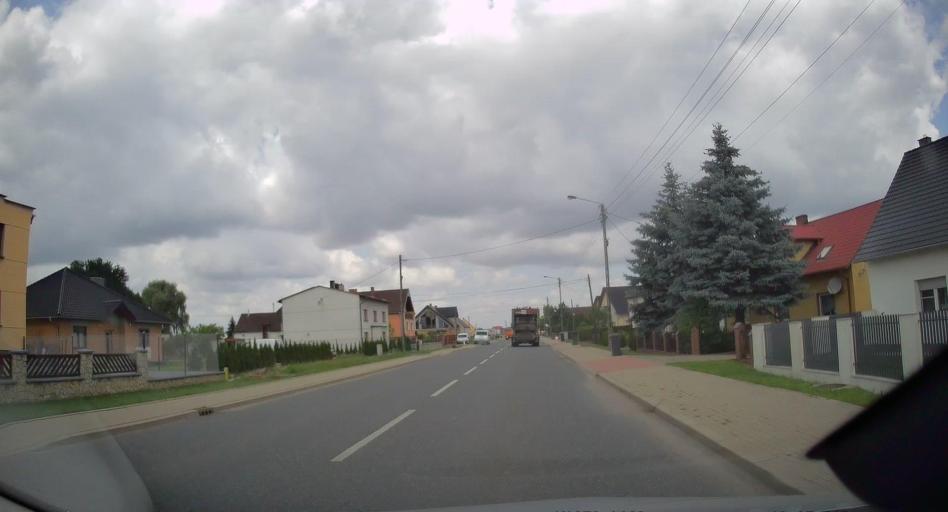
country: PL
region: Opole Voivodeship
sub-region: Powiat prudnicki
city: Glogowek
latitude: 50.3433
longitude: 17.9034
